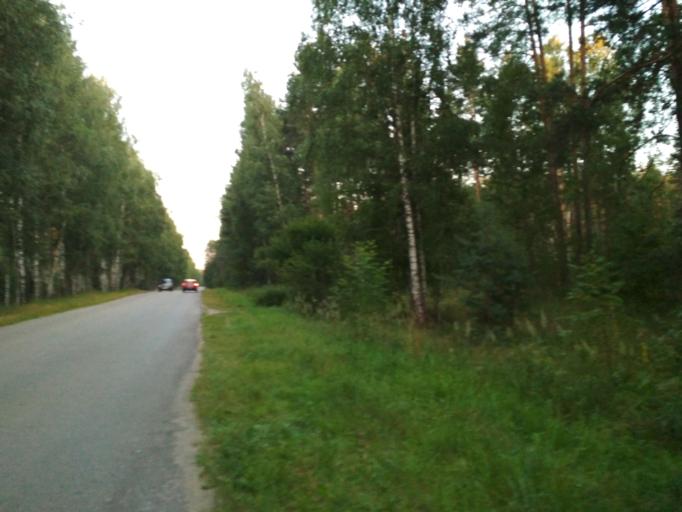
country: RU
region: Rjazan
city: Solotcha
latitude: 54.8285
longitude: 39.9423
